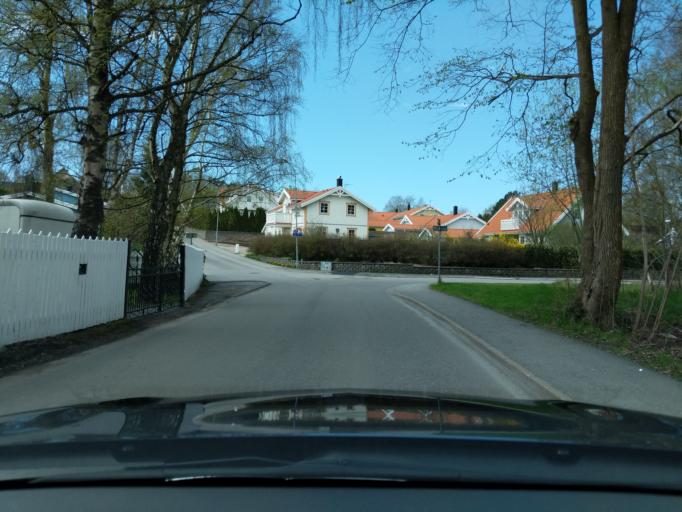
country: SE
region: Vaestra Goetaland
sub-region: Goteborg
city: Majorna
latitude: 57.6349
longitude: 11.9292
